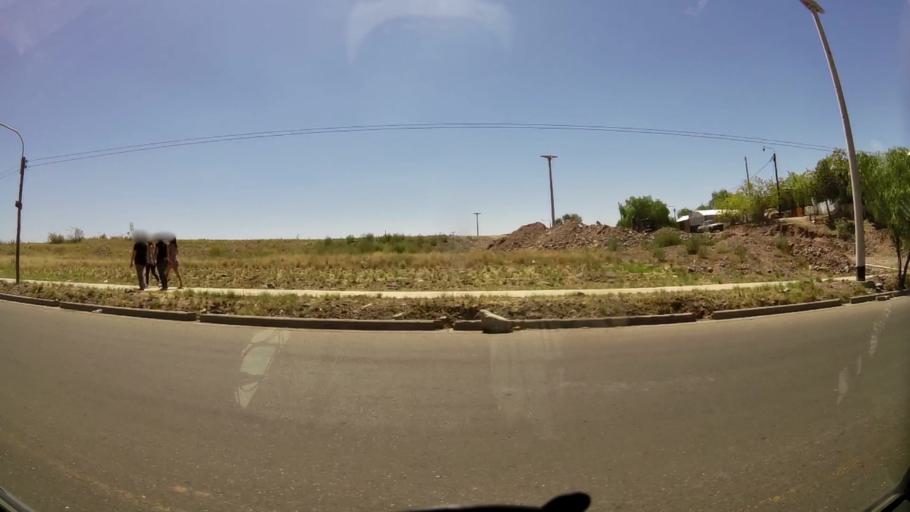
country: AR
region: Mendoza
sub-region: Departamento de Godoy Cruz
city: Godoy Cruz
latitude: -32.9463
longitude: -68.8646
